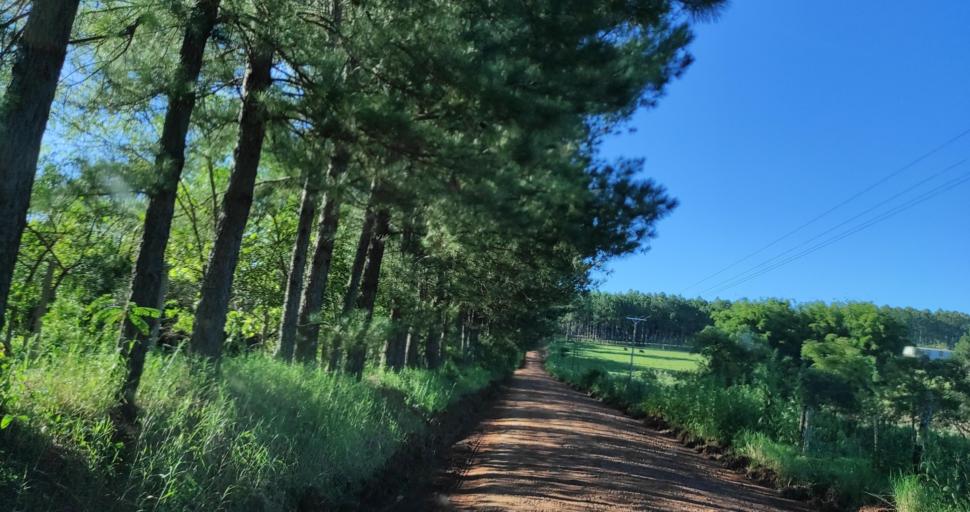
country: AR
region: Misiones
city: Puerto Rico
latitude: -26.8357
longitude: -55.0020
